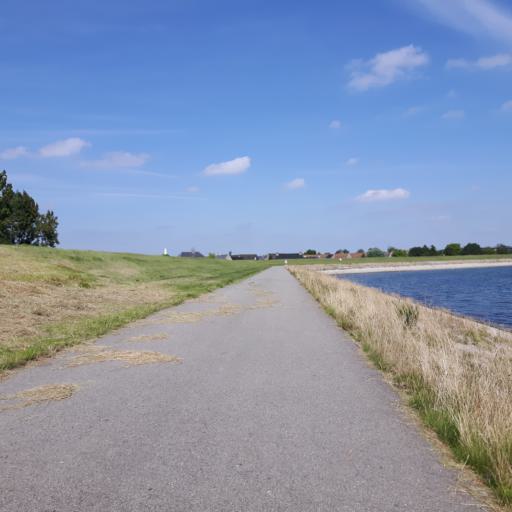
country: NL
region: North Brabant
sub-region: Gemeente Steenbergen
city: Nieuw-Vossemeer
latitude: 51.6135
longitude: 4.1586
